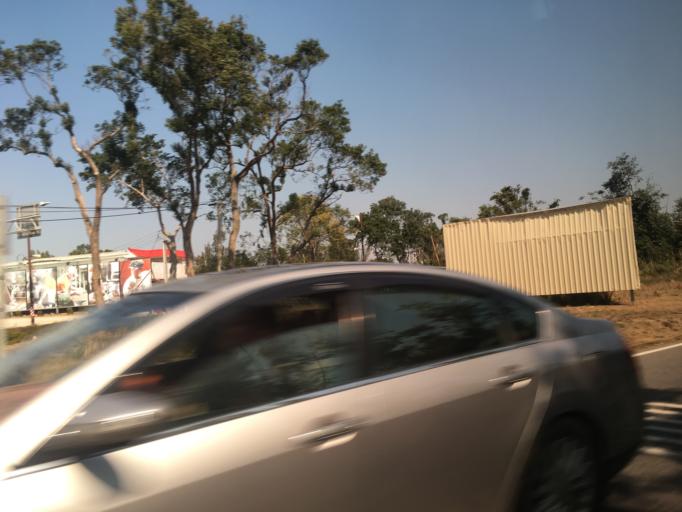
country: TW
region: Fukien
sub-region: Kinmen
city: Jincheng
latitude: 24.4325
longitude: 118.3250
